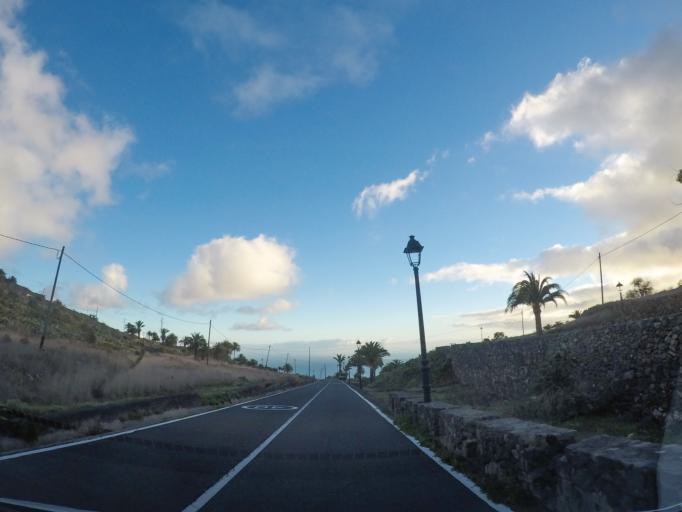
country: ES
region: Canary Islands
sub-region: Provincia de Santa Cruz de Tenerife
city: Alajero
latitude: 28.0691
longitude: -17.2388
